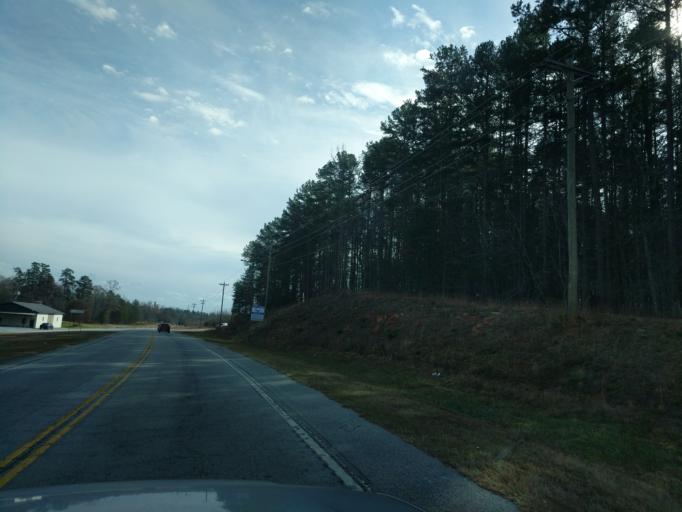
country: US
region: South Carolina
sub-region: Oconee County
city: Walhalla
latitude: 34.8295
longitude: -83.0464
